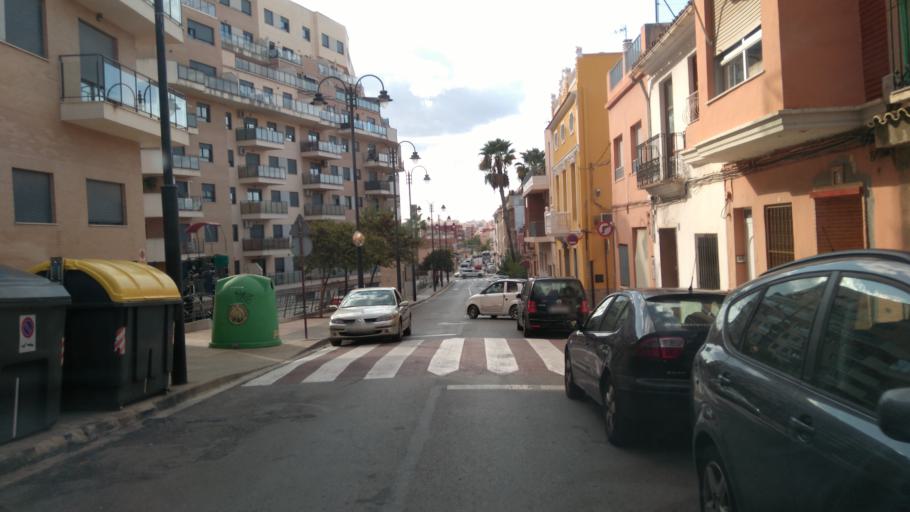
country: ES
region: Valencia
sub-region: Provincia de Valencia
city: Alzira
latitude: 39.1534
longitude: -0.4246
